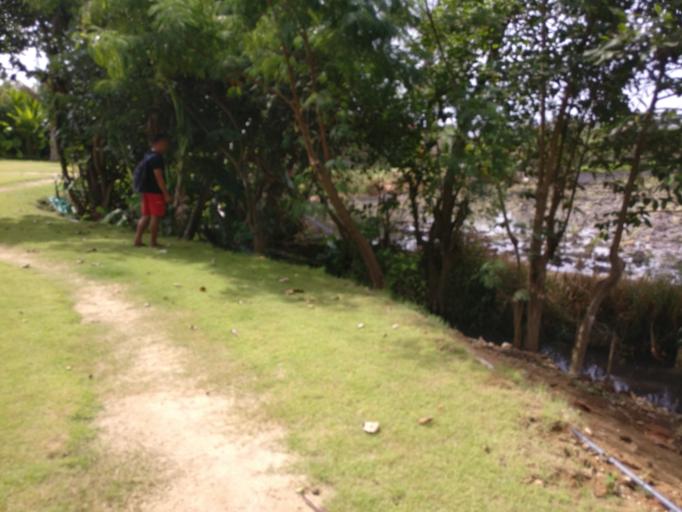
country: ID
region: Bali
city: Banjar Pasekan
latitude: -8.5965
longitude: 115.3383
